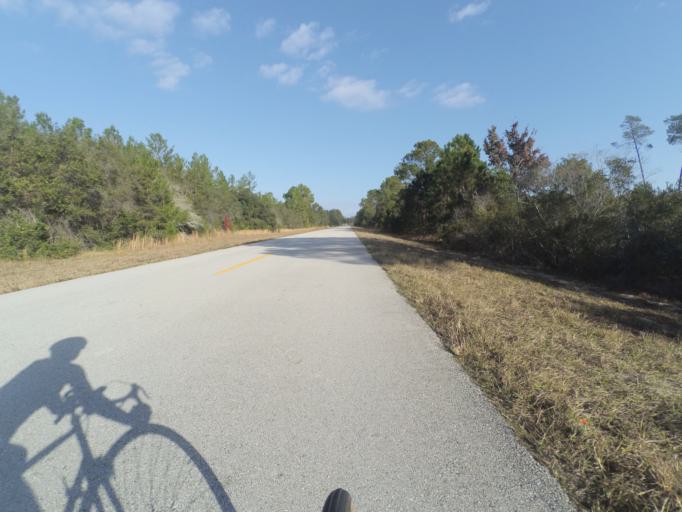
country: US
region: Florida
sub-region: Lake County
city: Astor
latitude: 29.1427
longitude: -81.5755
